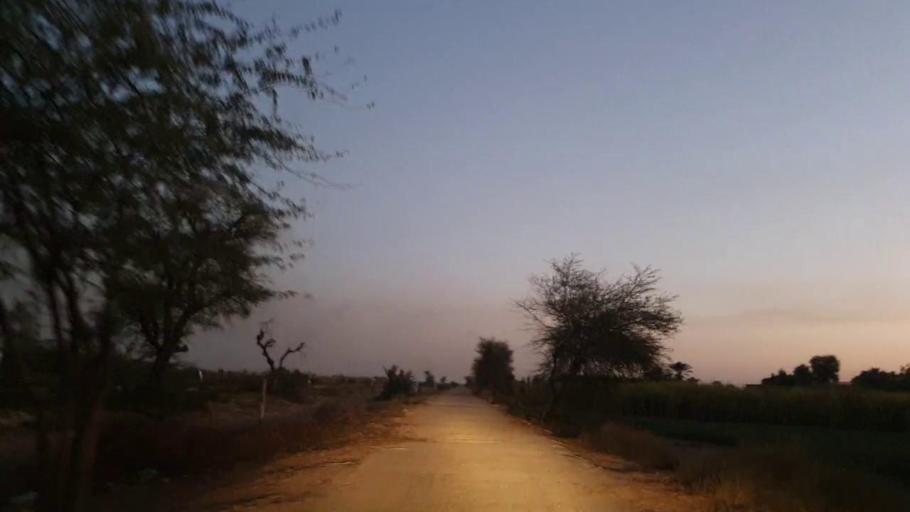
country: PK
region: Sindh
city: Nawabshah
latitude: 26.3404
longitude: 68.3711
